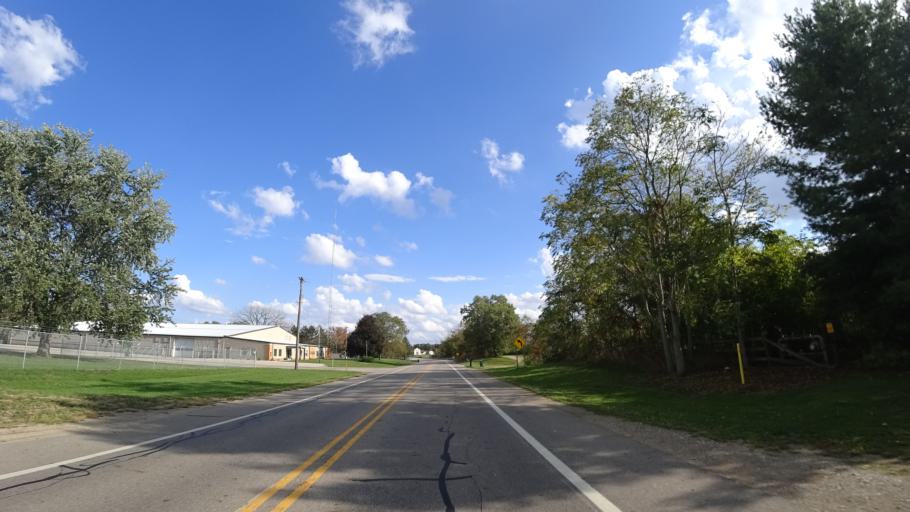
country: US
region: Michigan
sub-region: Saint Joseph County
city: Centreville
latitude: 41.9244
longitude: -85.5498
